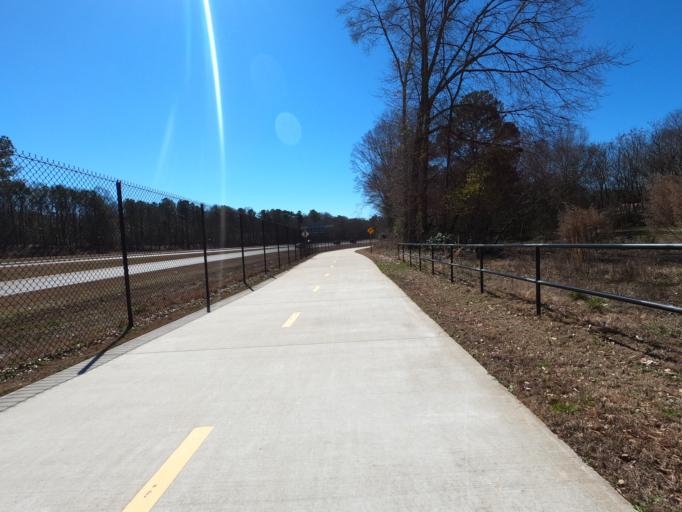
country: US
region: Georgia
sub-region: Clarke County
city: Athens
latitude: 33.9454
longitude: -83.3597
